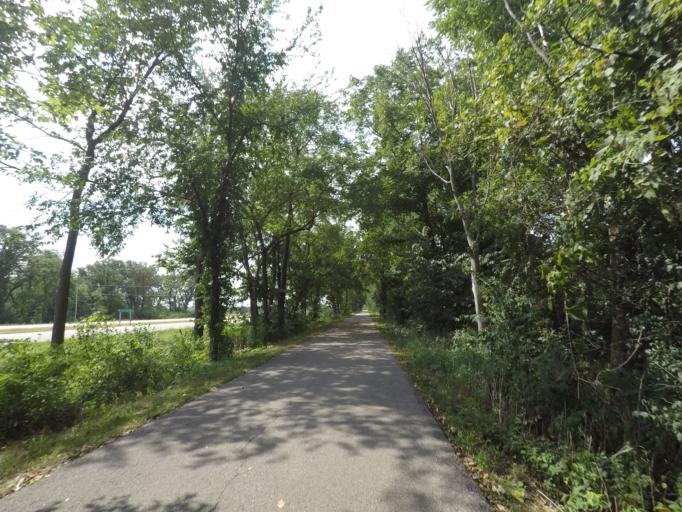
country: US
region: Wisconsin
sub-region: Jefferson County
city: Lake Koshkonong
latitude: 42.8628
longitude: -88.8998
